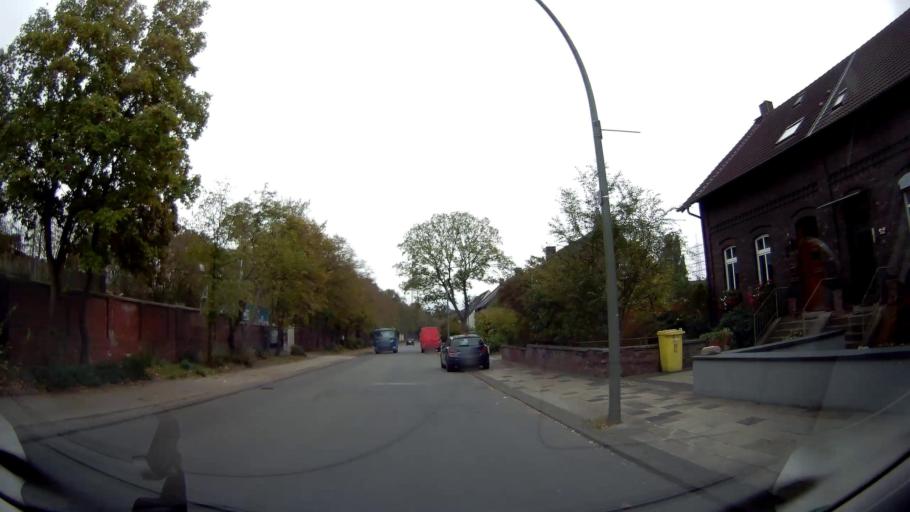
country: DE
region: North Rhine-Westphalia
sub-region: Regierungsbezirk Munster
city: Bottrop
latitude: 51.5177
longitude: 6.9588
